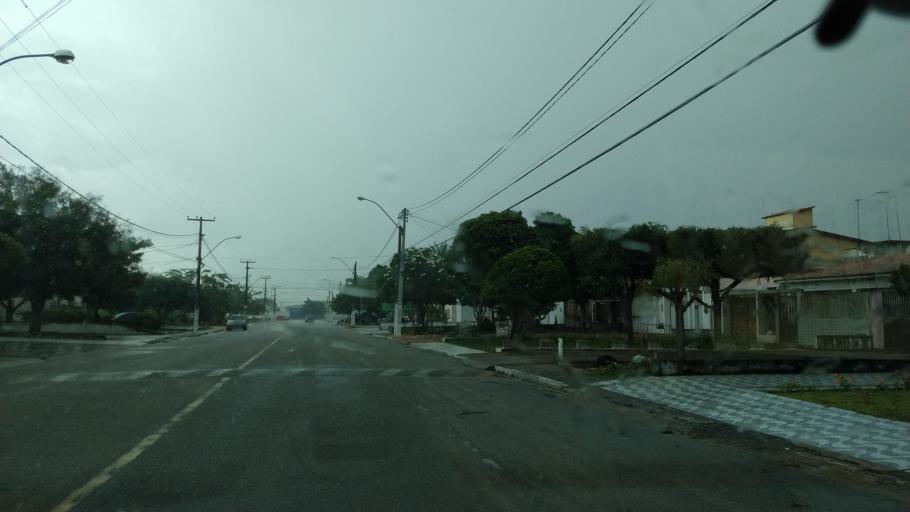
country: BR
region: Rio Grande do Norte
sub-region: Parnamirim
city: Parnamirim
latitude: -5.9219
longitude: -35.2680
